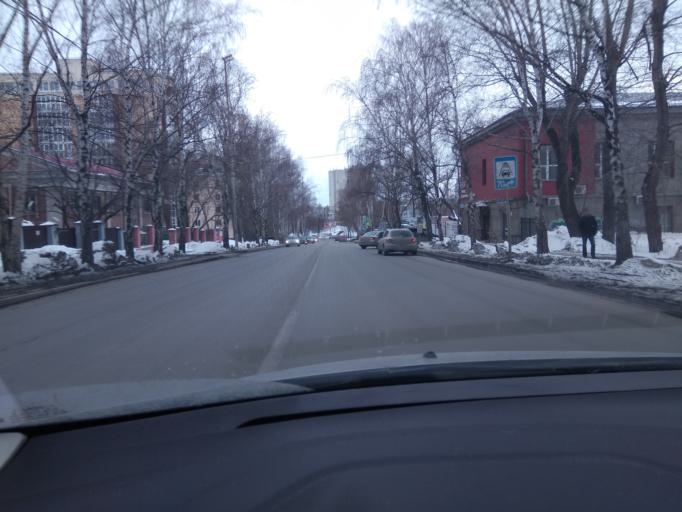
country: RU
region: Sverdlovsk
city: Yekaterinburg
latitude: 56.8464
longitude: 60.6340
